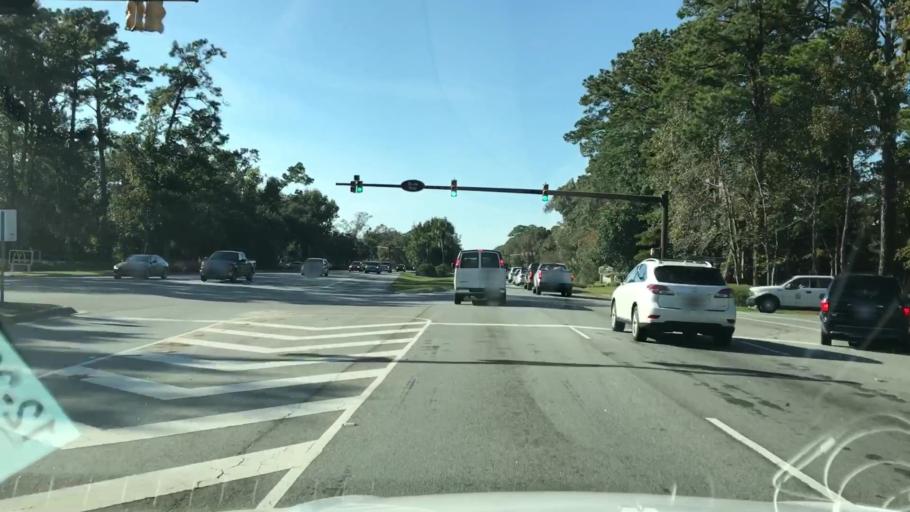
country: US
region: South Carolina
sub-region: Beaufort County
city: Hilton Head Island
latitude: 32.2149
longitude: -80.7000
